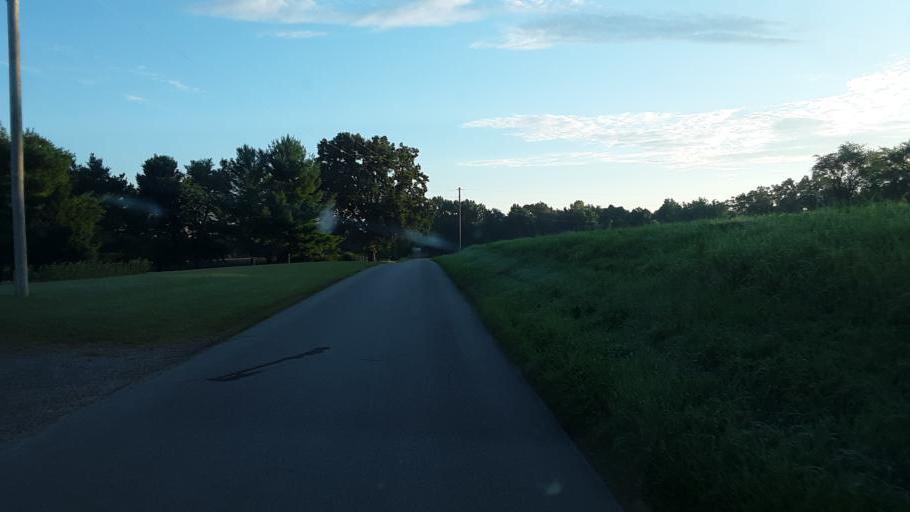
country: US
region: Kentucky
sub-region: Todd County
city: Guthrie
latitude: 36.6899
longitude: -87.1710
